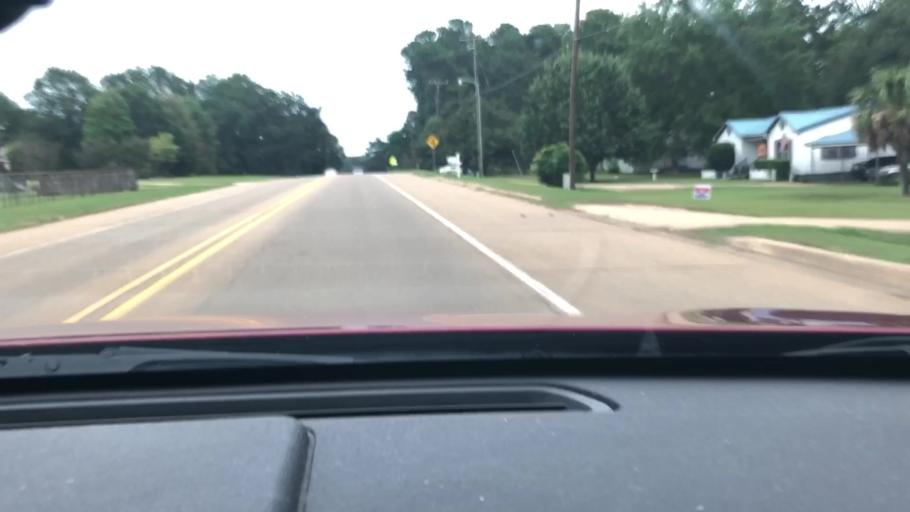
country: US
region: Arkansas
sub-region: Lafayette County
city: Stamps
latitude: 33.3651
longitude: -93.4835
